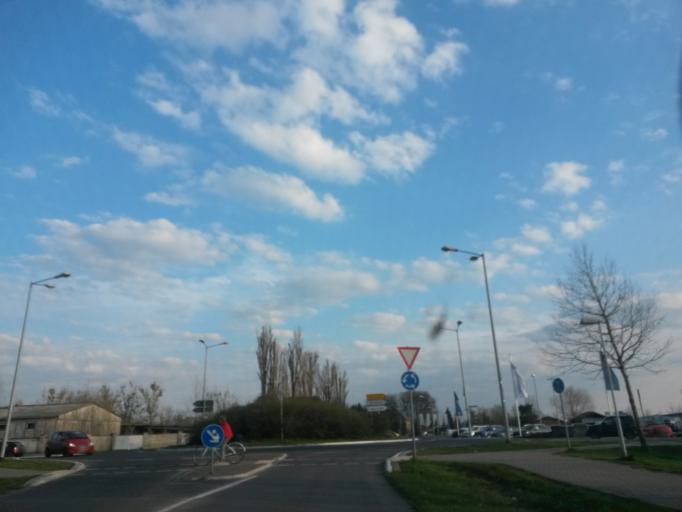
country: DE
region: Brandenburg
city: Strausberg
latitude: 52.5920
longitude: 13.9093
